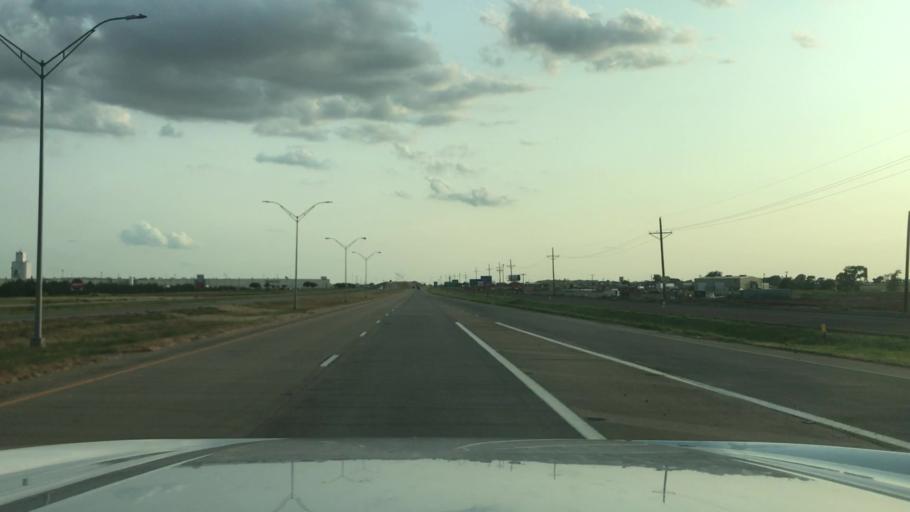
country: US
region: Texas
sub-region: Hale County
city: Seth Ward
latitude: 34.2187
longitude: -101.7263
